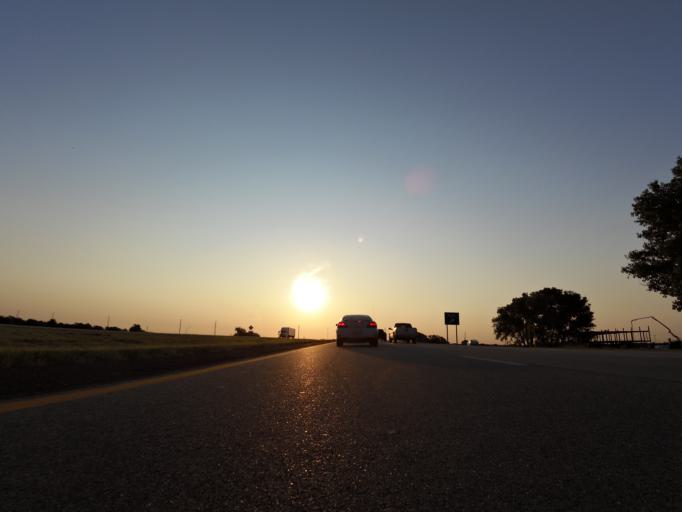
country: US
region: Kansas
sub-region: Sedgwick County
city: Maize
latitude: 37.7596
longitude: -97.4295
